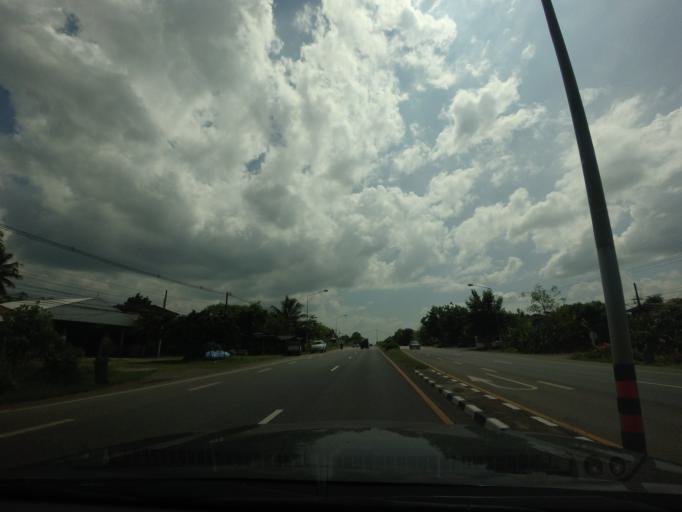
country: TH
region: Phetchabun
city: Phetchabun
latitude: 16.2205
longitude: 101.0891
